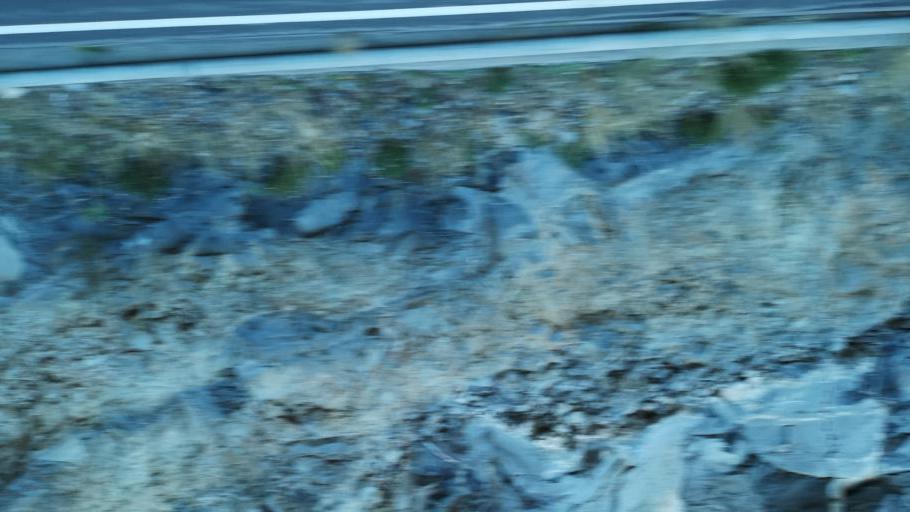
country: ES
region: Canary Islands
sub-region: Provincia de Santa Cruz de Tenerife
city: Alajero
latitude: 28.0313
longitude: -17.2037
